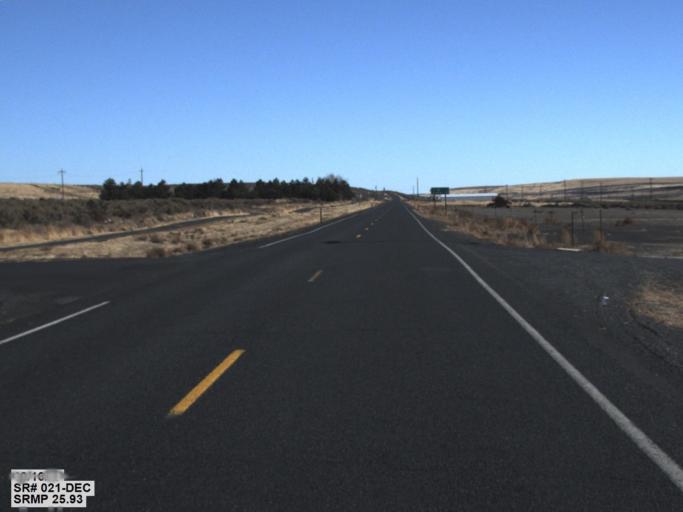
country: US
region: Washington
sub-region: Adams County
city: Ritzville
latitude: 46.9708
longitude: -118.5996
